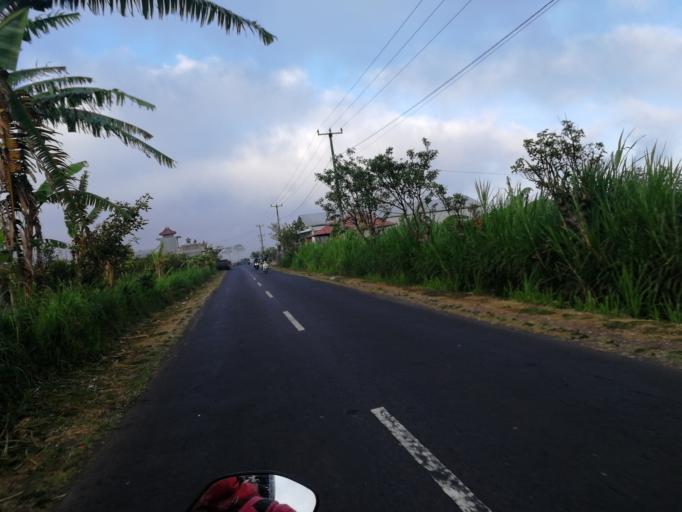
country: ID
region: Bali
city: Banjar Kedisan
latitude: -8.2226
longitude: 115.2633
